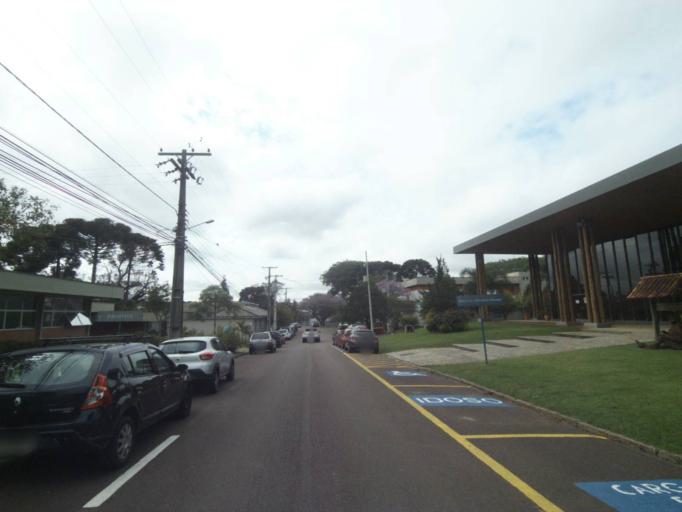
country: BR
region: Parana
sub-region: Curitiba
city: Curitiba
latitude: -25.4133
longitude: -49.2491
